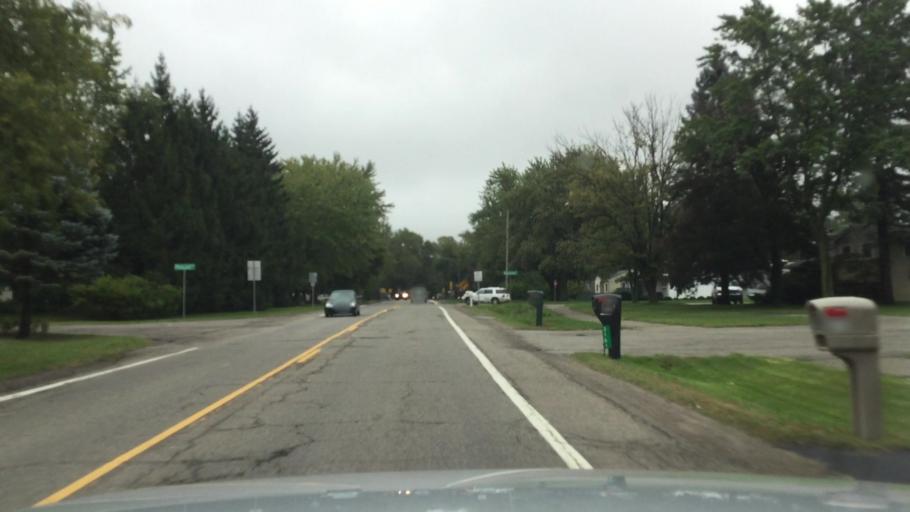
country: US
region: Michigan
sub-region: Oakland County
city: Waterford
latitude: 42.6840
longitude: -83.4082
